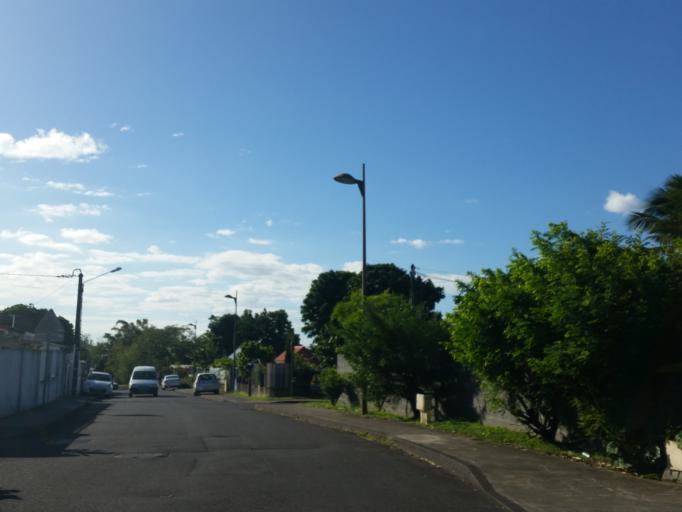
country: RE
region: Reunion
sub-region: Reunion
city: Saint-Andre
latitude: -20.9699
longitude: 55.6588
